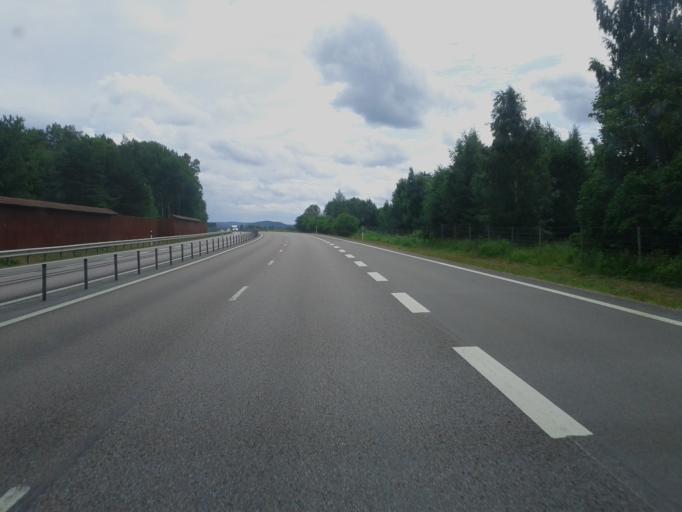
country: SE
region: Dalarna
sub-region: Borlange Kommun
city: Ornas
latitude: 60.4354
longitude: 15.5129
